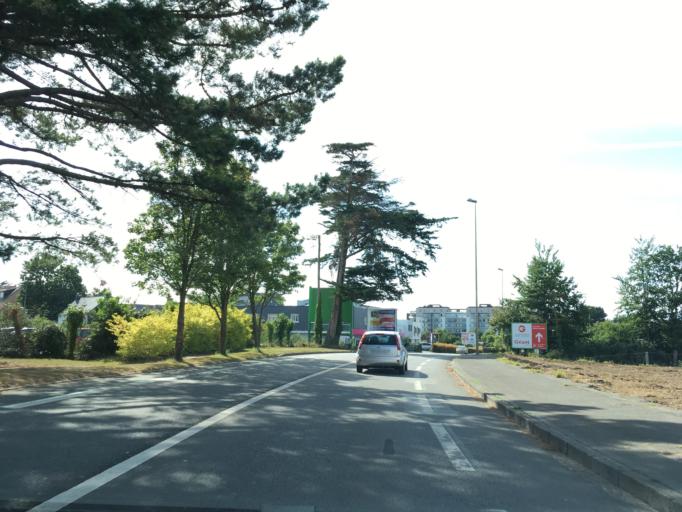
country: FR
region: Brittany
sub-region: Departement du Morbihan
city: Lorient
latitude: 47.7521
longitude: -3.3800
